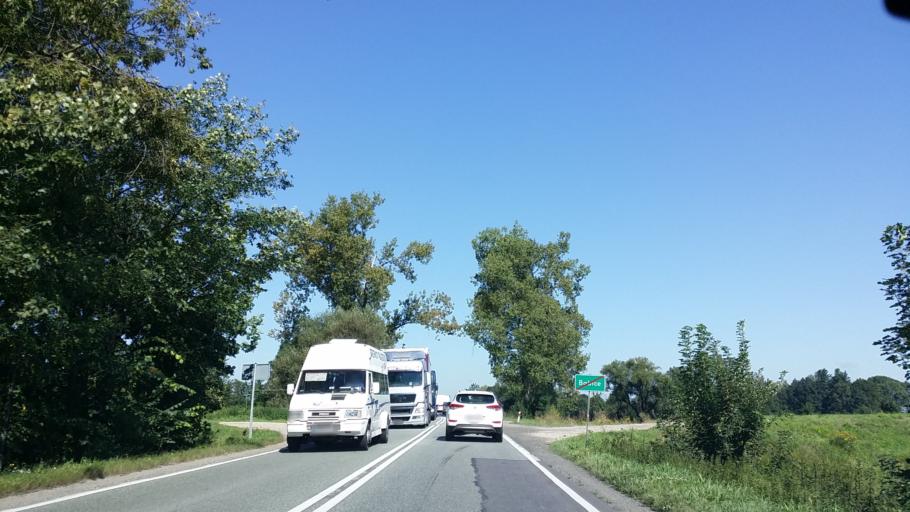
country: PL
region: Lesser Poland Voivodeship
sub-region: Powiat oswiecimski
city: Babice
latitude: 50.0625
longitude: 19.1936
